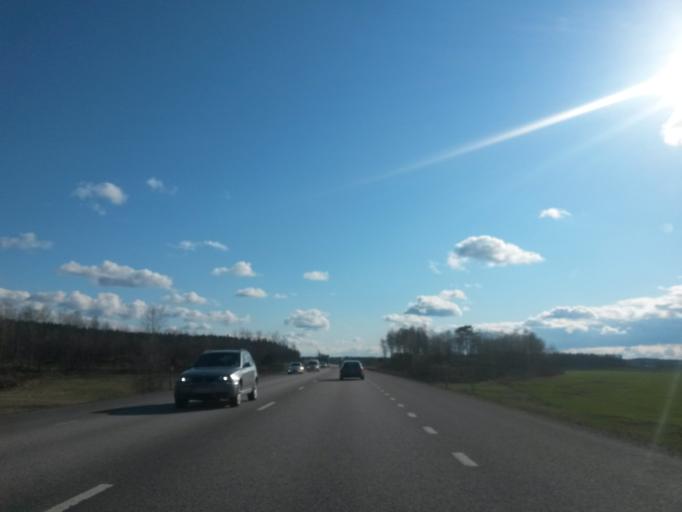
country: SE
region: Vaestra Goetaland
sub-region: Vargarda Kommun
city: Vargarda
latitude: 58.1183
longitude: 12.8470
